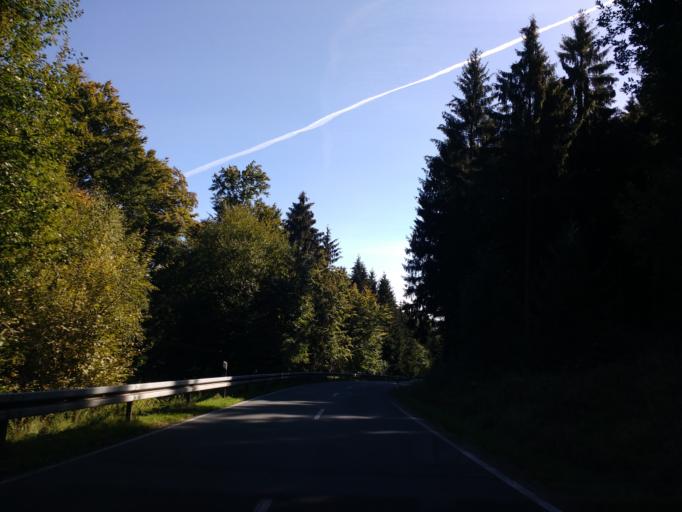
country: DE
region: North Rhine-Westphalia
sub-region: Regierungsbezirk Detmold
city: Willebadessen
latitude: 51.6203
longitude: 9.0018
